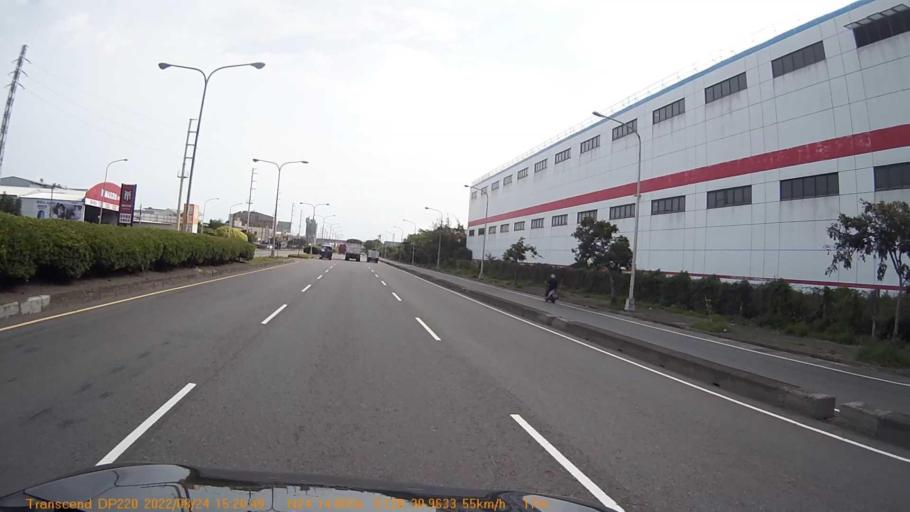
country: TW
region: Taiwan
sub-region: Changhua
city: Chang-hua
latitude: 24.2338
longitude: 120.5159
